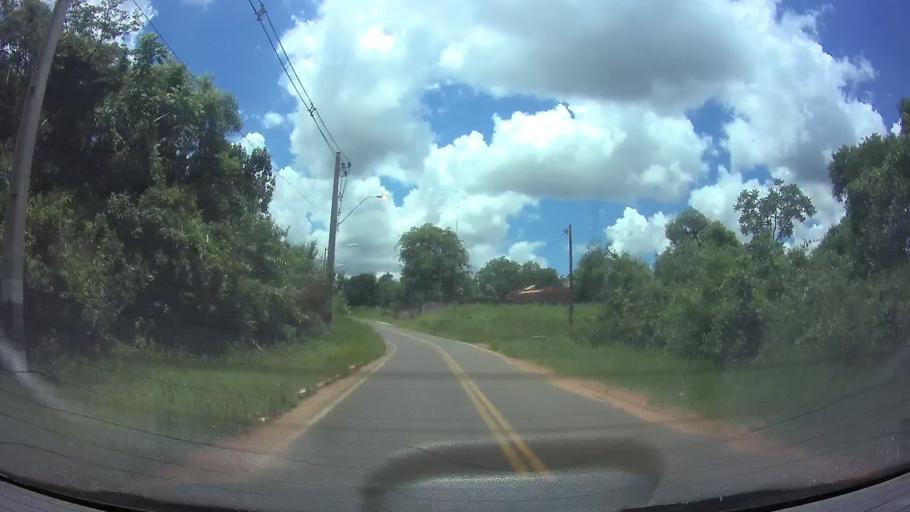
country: PY
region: Central
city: Capiata
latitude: -25.3162
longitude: -57.4310
